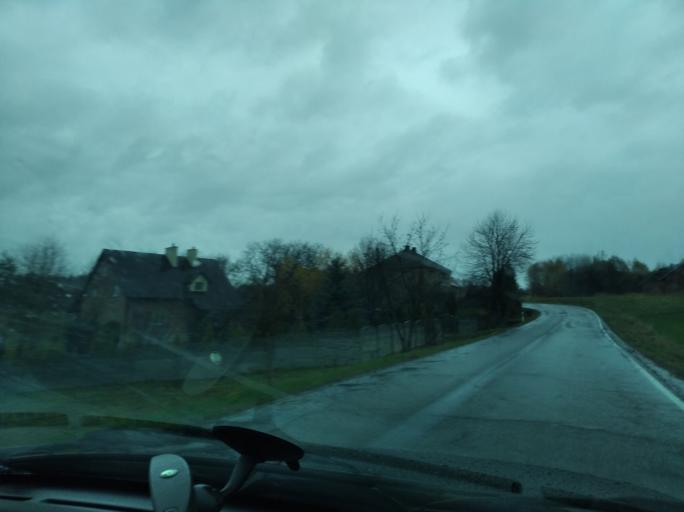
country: PL
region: Subcarpathian Voivodeship
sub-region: Powiat lancucki
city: Handzlowka
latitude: 49.9816
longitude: 22.1922
